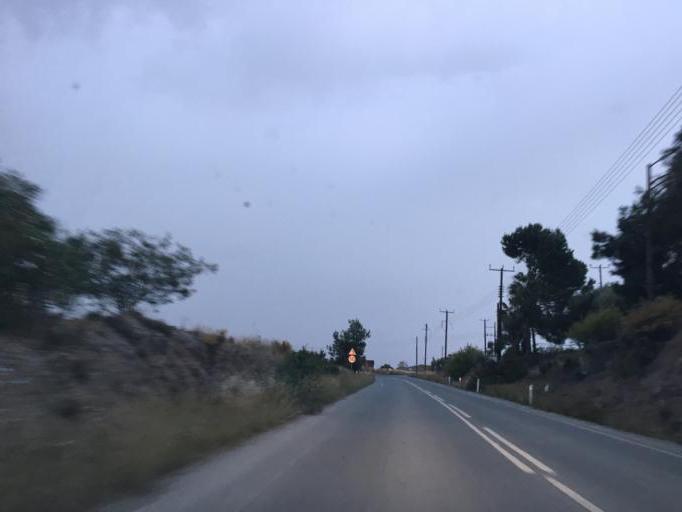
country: CY
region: Limassol
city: Parekklisha
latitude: 34.7575
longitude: 33.1599
